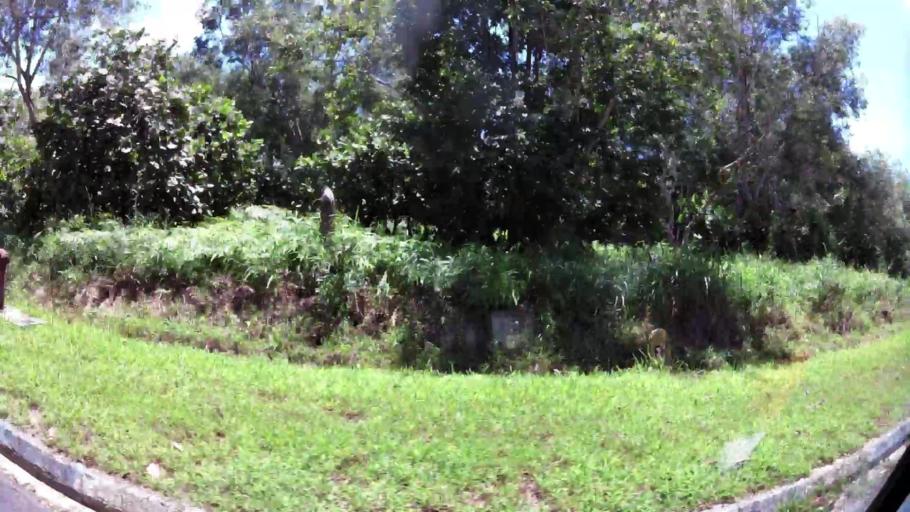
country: BN
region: Brunei and Muara
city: Bandar Seri Begawan
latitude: 4.9192
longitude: 114.9588
